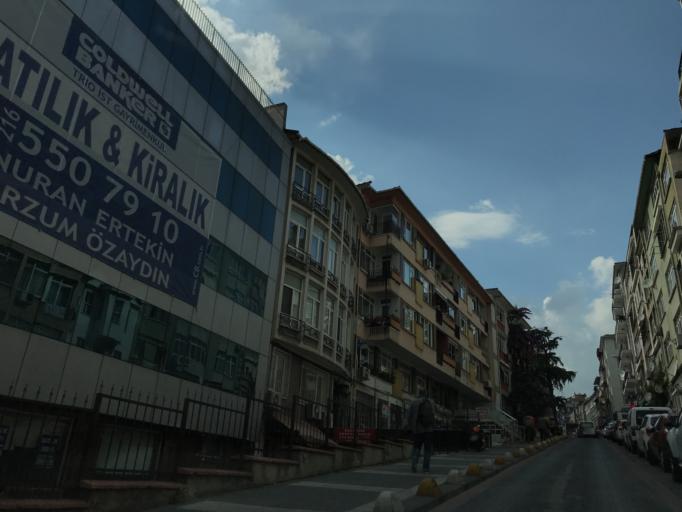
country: TR
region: Istanbul
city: UEskuedar
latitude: 40.9883
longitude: 29.0318
